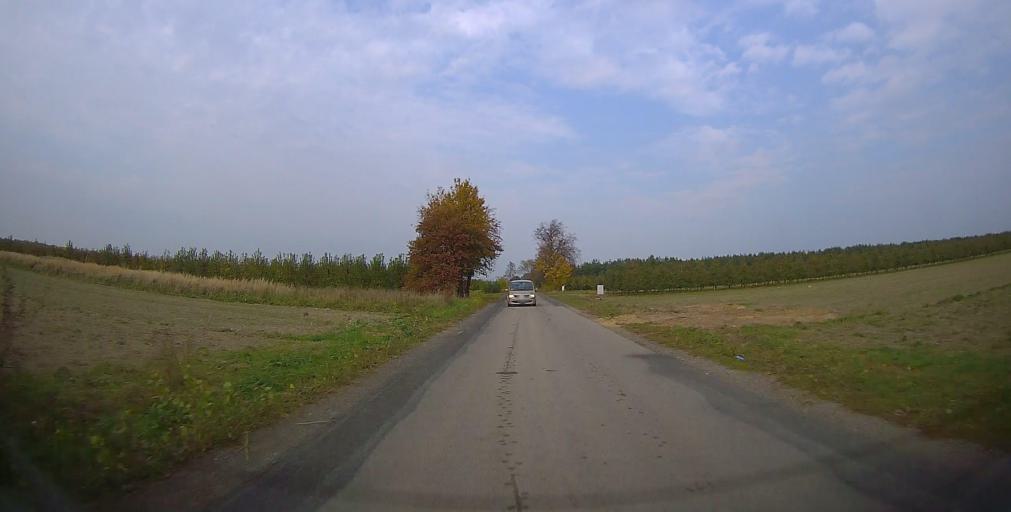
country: PL
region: Masovian Voivodeship
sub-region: Powiat grojecki
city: Mogielnica
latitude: 51.6523
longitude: 20.7245
